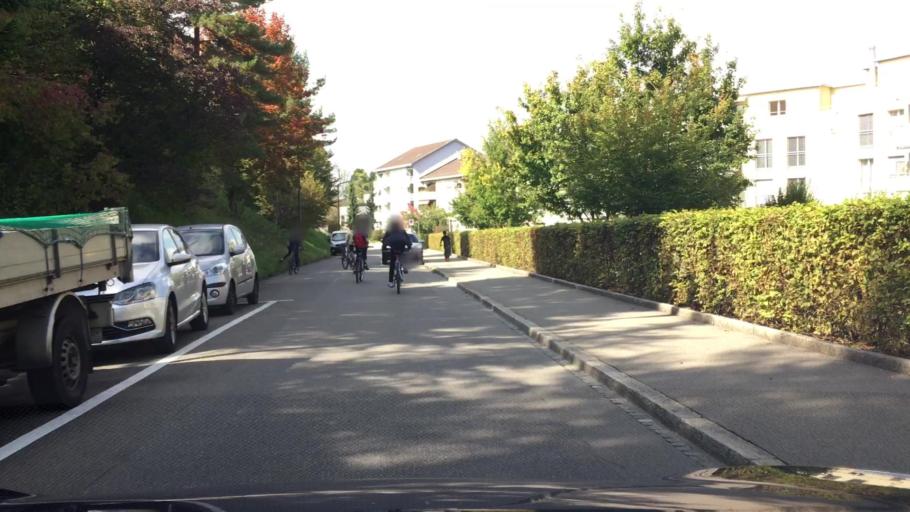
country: CH
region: Zurich
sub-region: Bezirk Winterthur
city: Seen (Kreis 3) / Bueelwiesen
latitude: 47.4808
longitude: 8.7679
